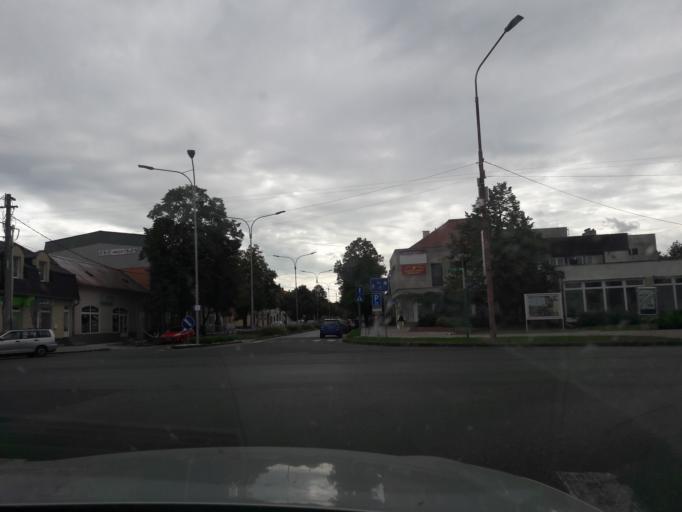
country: SK
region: Nitriansky
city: Surany
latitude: 48.0889
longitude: 18.1846
